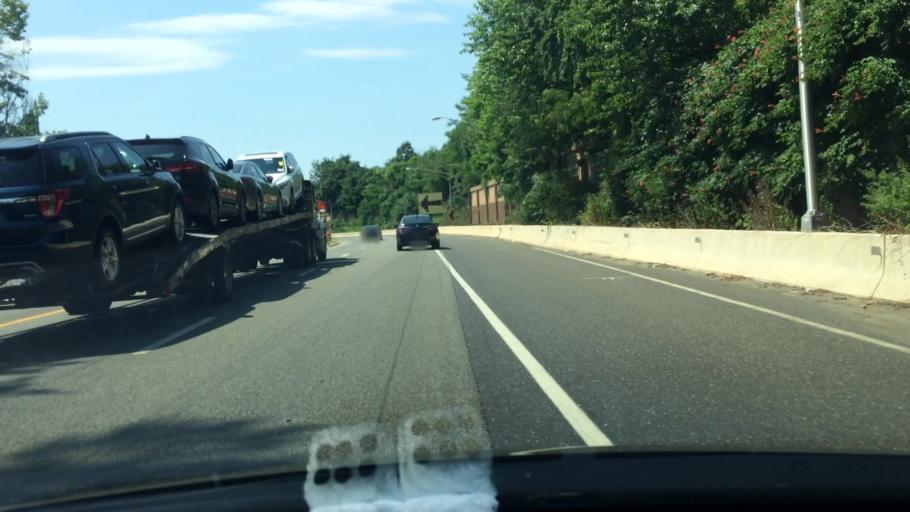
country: US
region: New Jersey
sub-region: Camden County
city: Mount Ephraim
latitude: 39.8774
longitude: -75.1003
